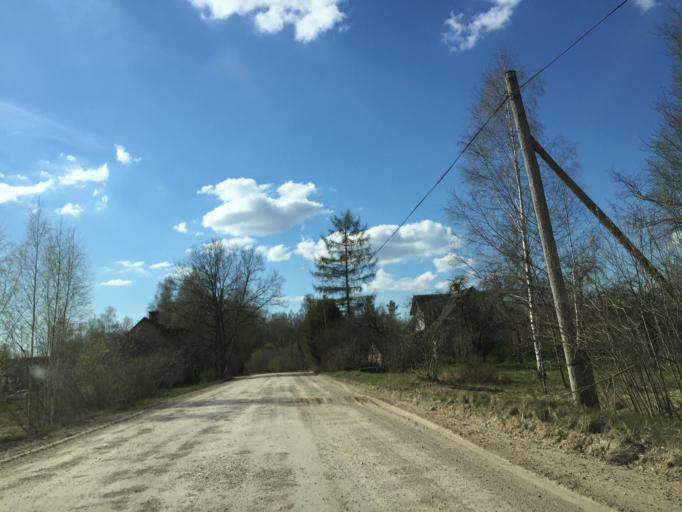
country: LV
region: Seja
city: Loja
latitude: 57.3452
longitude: 24.5957
